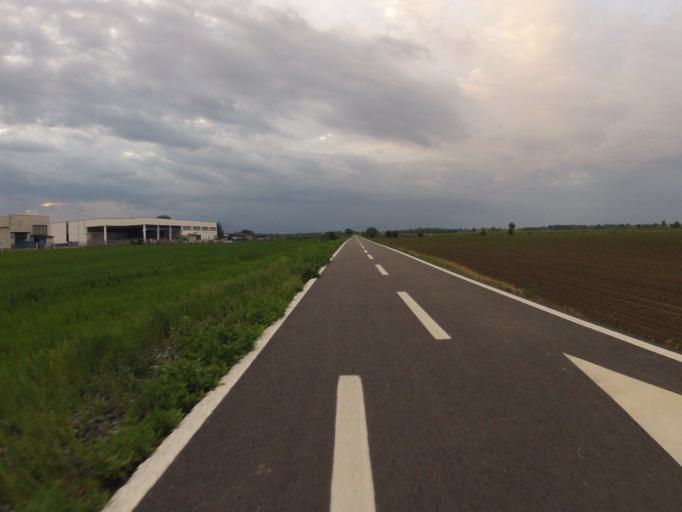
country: IT
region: Piedmont
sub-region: Provincia di Torino
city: Villafranca Piemonte
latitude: 44.7921
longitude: 7.5078
